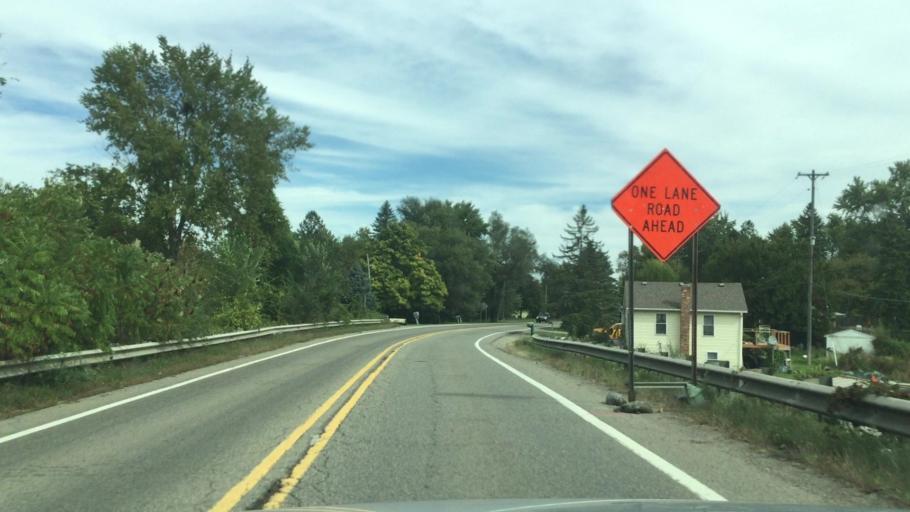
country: US
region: Michigan
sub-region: Oakland County
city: Holly
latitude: 42.8094
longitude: -83.6167
